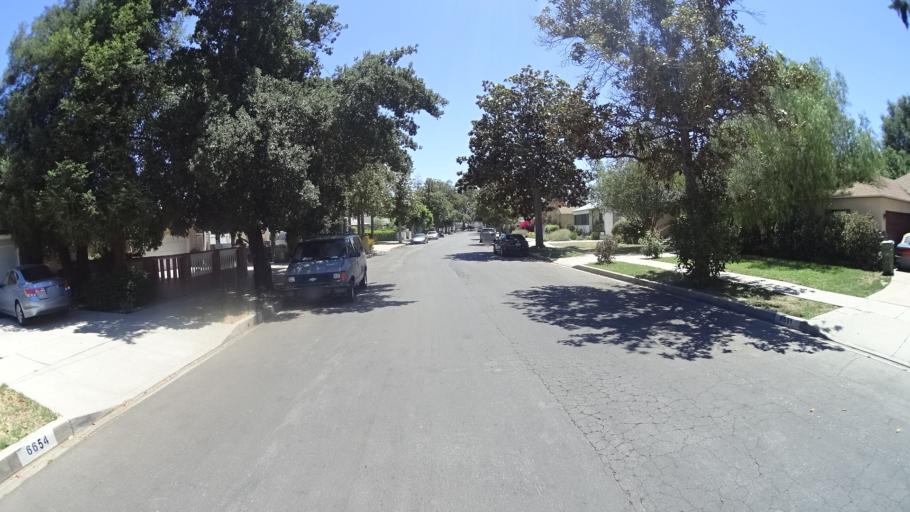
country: US
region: California
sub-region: Los Angeles County
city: Northridge
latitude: 34.1920
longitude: -118.5283
